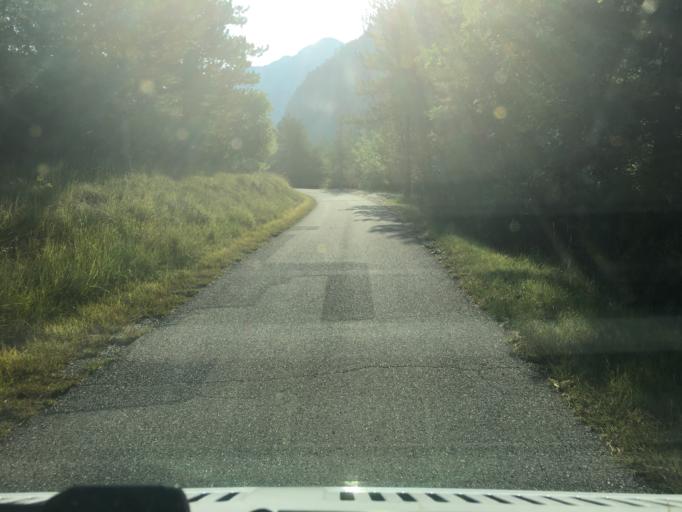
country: FR
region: Provence-Alpes-Cote d'Azur
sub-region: Departement des Alpes-de-Haute-Provence
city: Mallemoisson
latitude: 43.9478
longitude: 6.2203
